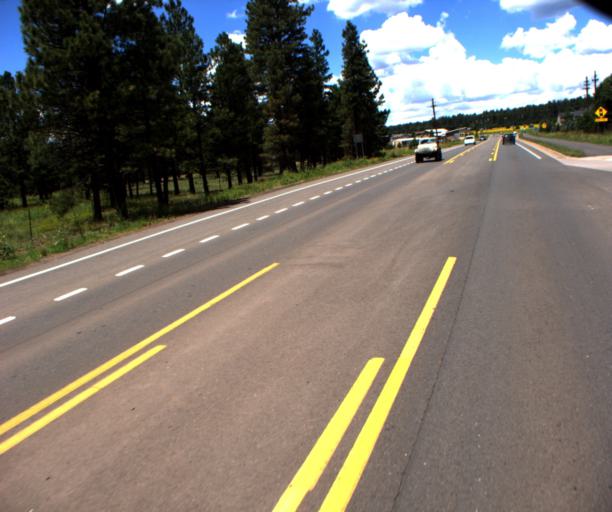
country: US
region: Arizona
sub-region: Coconino County
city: Flagstaff
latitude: 35.2359
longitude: -111.6659
